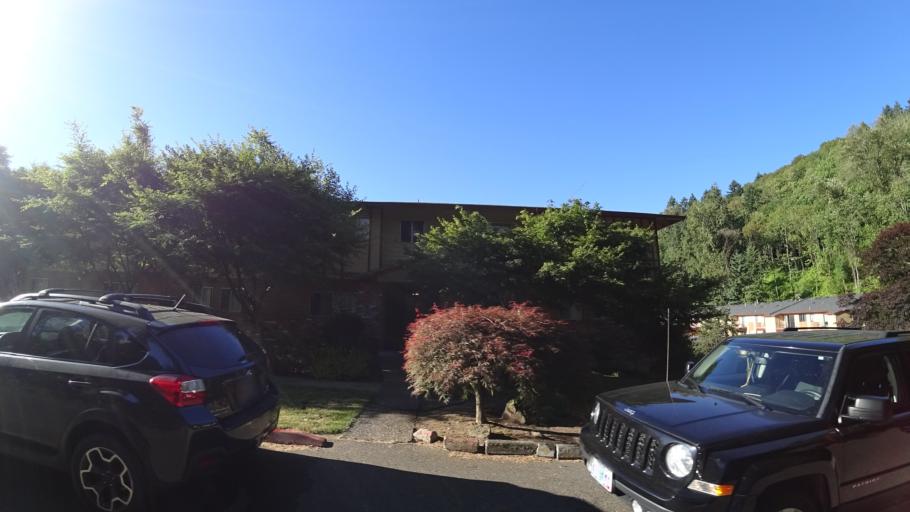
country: US
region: Oregon
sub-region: Multnomah County
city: Portland
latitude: 45.4871
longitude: -122.6809
